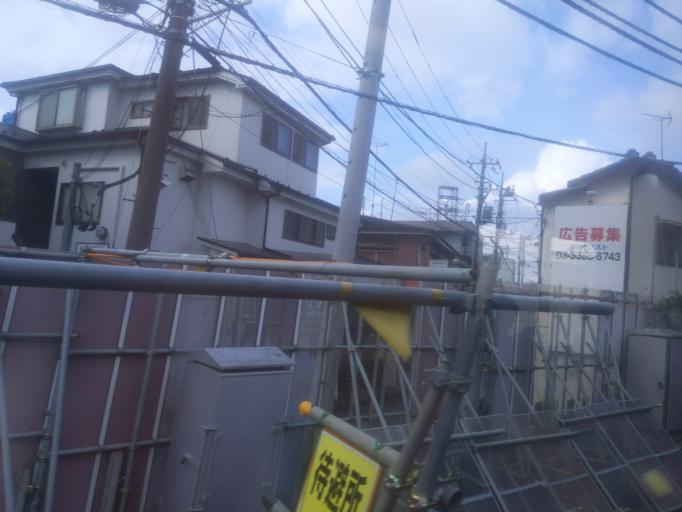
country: JP
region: Tokyo
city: Tokyo
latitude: 35.7195
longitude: 139.6632
